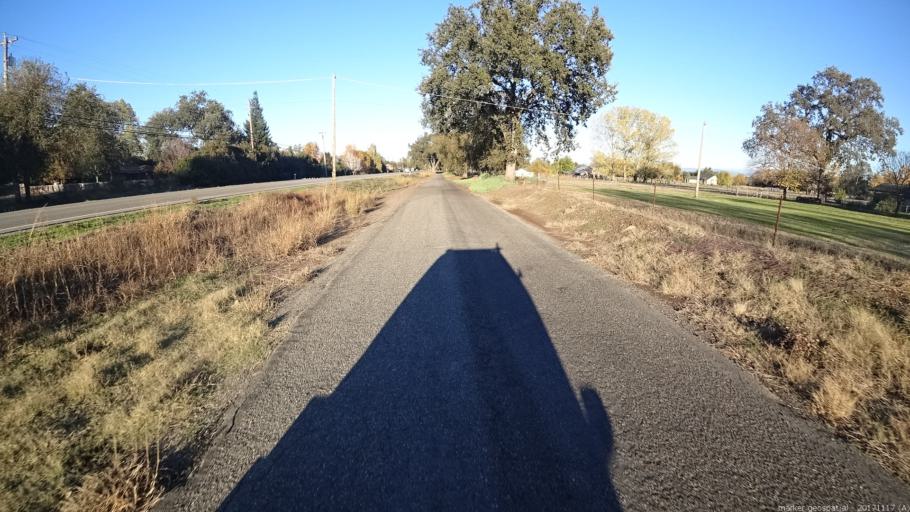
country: US
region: California
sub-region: Shasta County
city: Anderson
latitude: 40.4527
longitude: -122.2514
